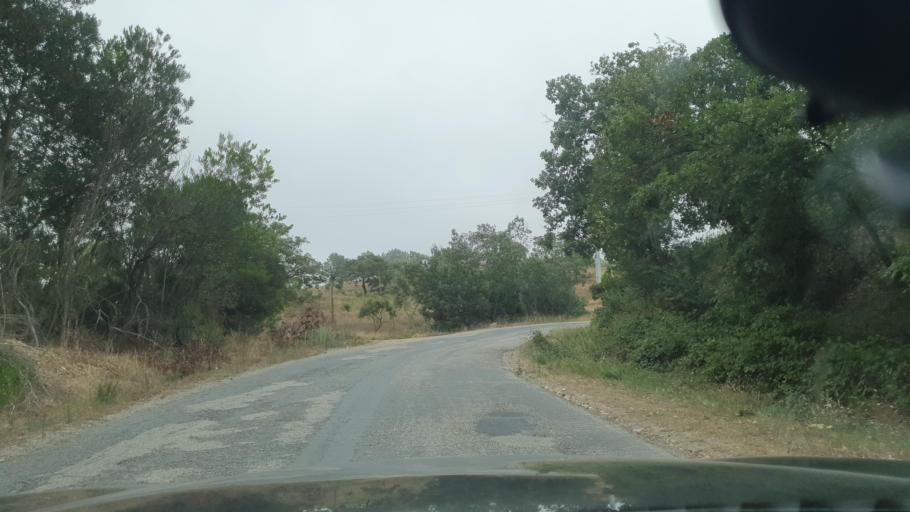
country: PT
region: Beja
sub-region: Odemira
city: Sao Teotonio
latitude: 37.5106
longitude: -8.6973
